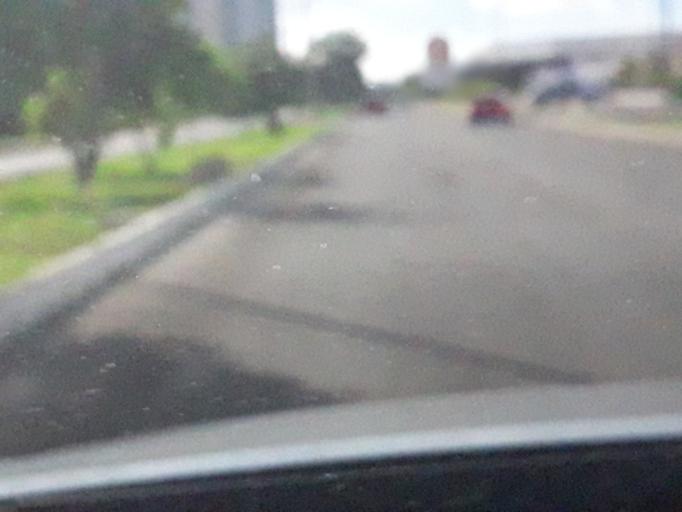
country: MX
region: Yucatan
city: Merida
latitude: 21.0375
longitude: -89.6122
